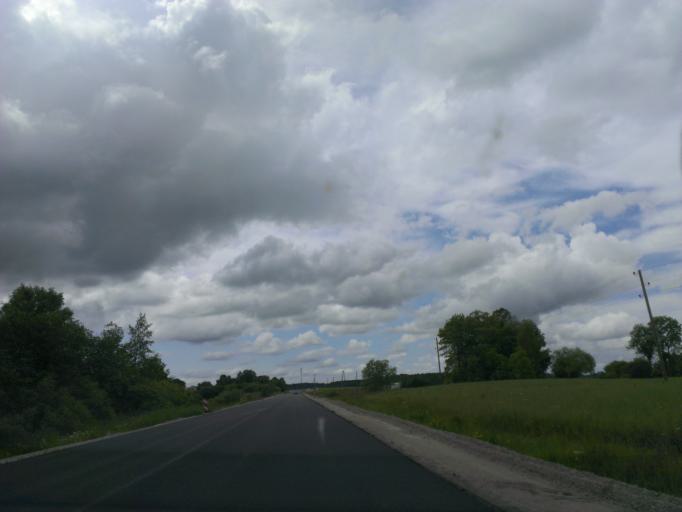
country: LV
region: Durbe
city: Liegi
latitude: 56.5890
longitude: 21.4254
